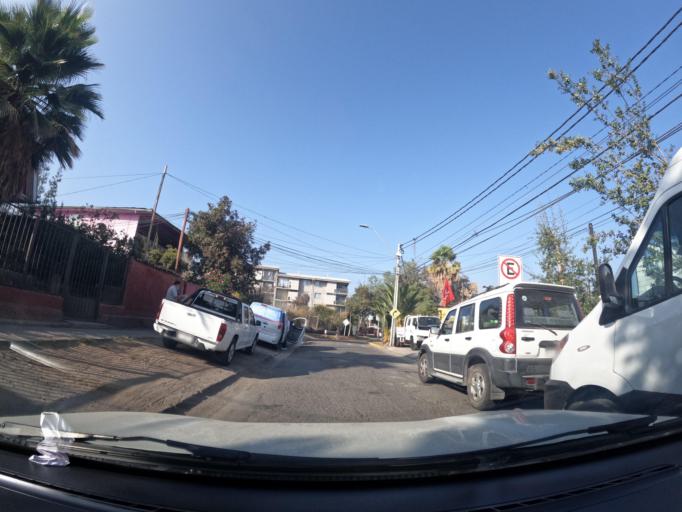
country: CL
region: Santiago Metropolitan
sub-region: Provincia de Santiago
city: Villa Presidente Frei, Nunoa, Santiago, Chile
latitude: -33.4689
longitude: -70.5336
